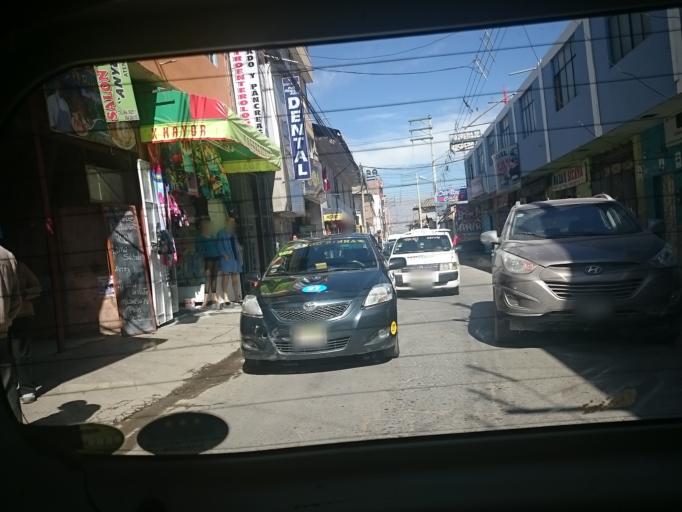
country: PE
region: Junin
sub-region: Provincia de Huancayo
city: Huancayo
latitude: -12.0729
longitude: -75.2084
